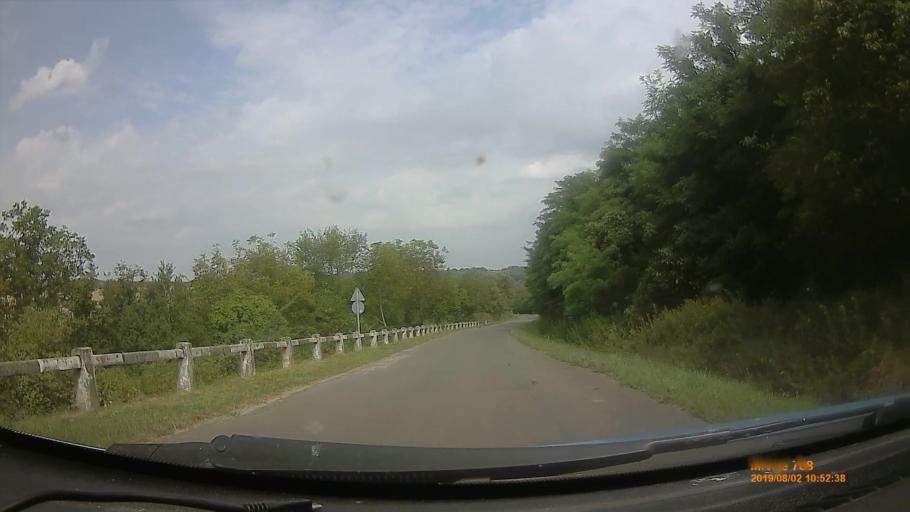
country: HU
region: Baranya
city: Buekkoesd
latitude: 46.0904
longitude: 17.9592
